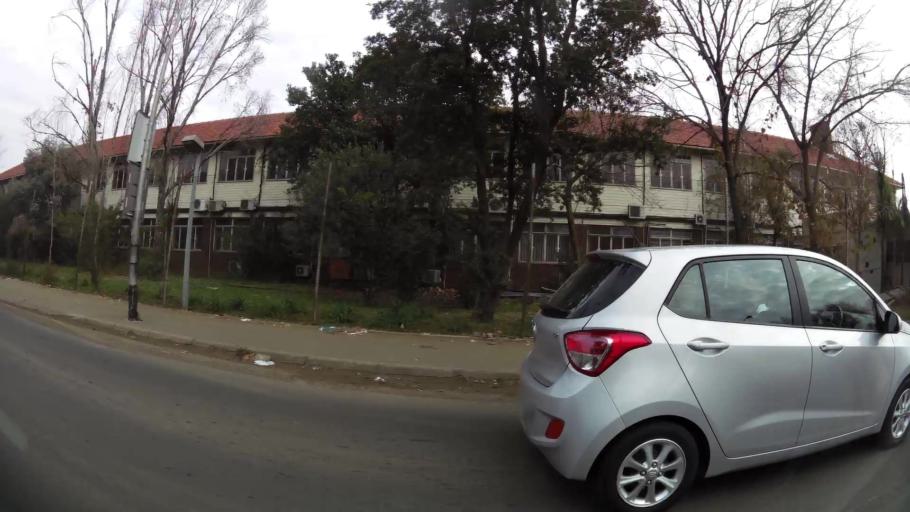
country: ZA
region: Orange Free State
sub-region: Mangaung Metropolitan Municipality
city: Bloemfontein
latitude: -29.1205
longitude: 26.2124
